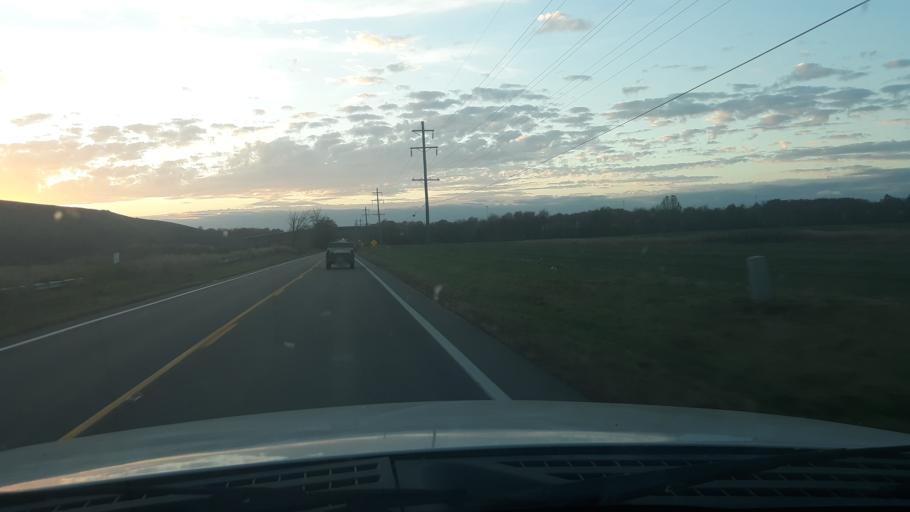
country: US
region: Illinois
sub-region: Saline County
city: Harrisburg
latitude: 37.8347
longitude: -88.5744
